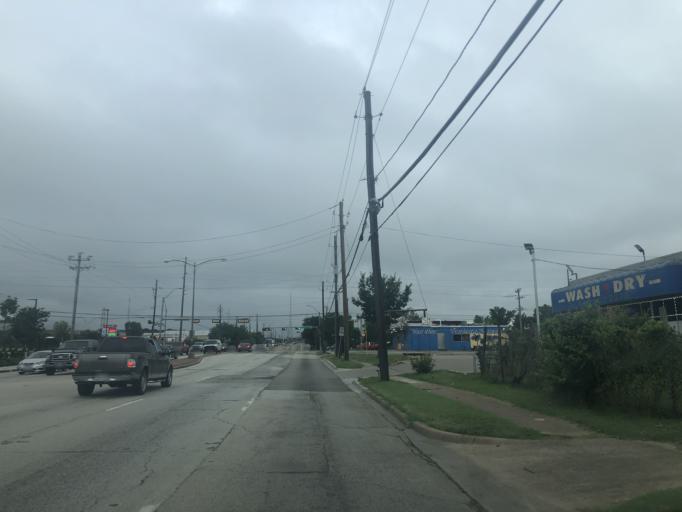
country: US
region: Texas
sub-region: Dallas County
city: Cockrell Hill
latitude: 32.7798
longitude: -96.8739
